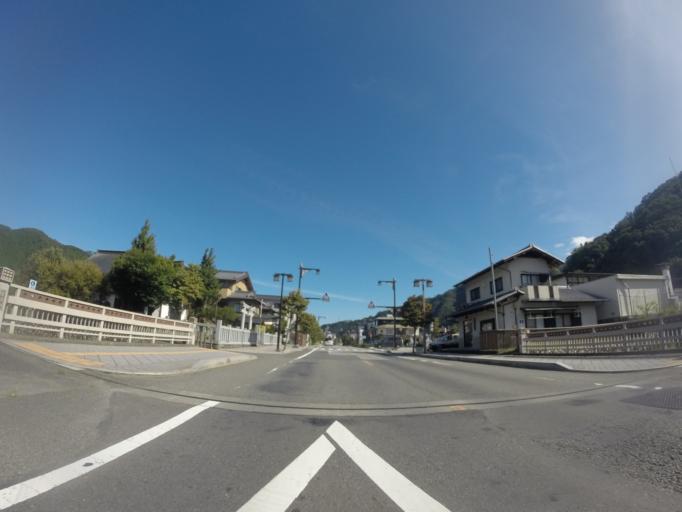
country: JP
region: Shizuoka
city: Fujinomiya
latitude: 35.3604
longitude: 138.4523
